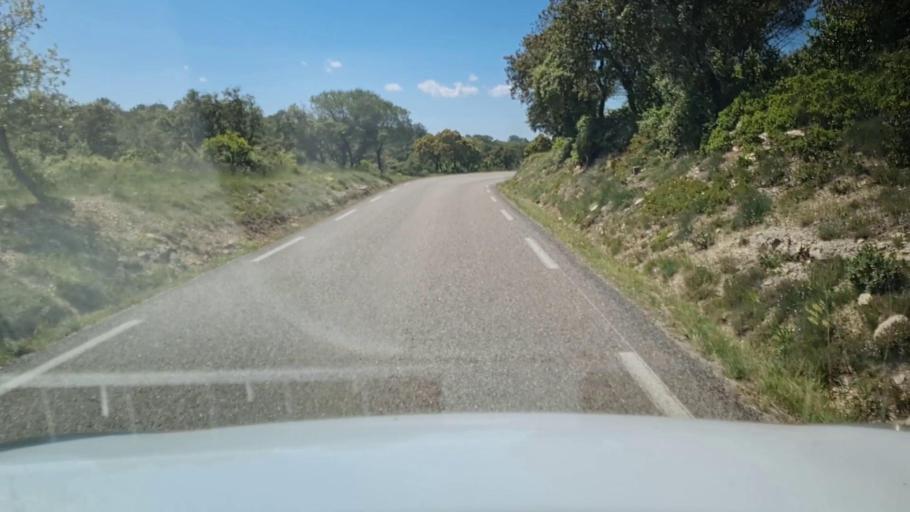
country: FR
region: Languedoc-Roussillon
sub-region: Departement du Gard
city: Clarensac
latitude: 43.8438
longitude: 4.2301
